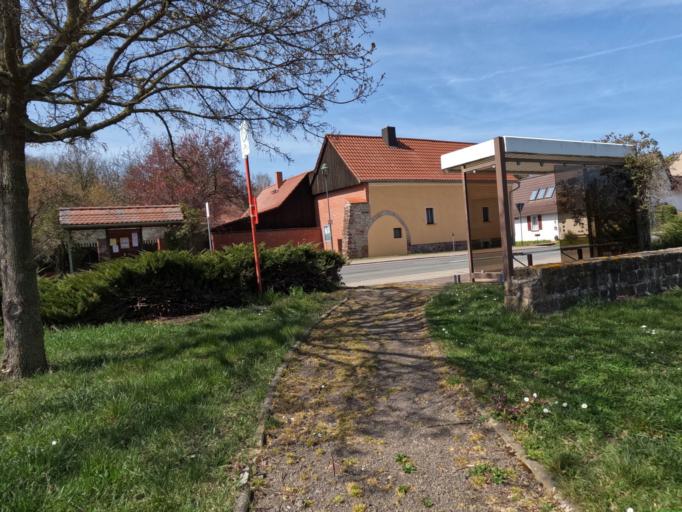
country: DE
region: Saxony-Anhalt
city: Beesenstedt
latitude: 51.6017
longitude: 11.7503
